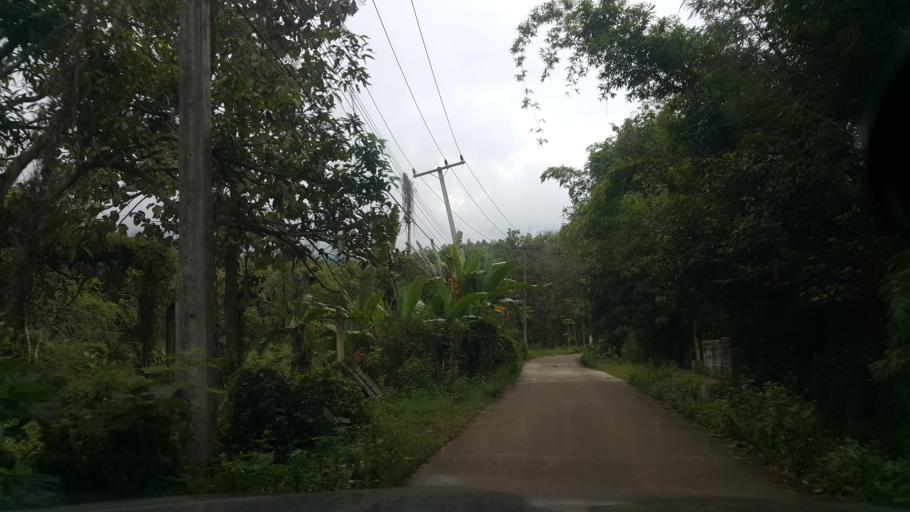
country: TH
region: Chiang Mai
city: Mae On
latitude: 18.7722
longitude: 99.2626
